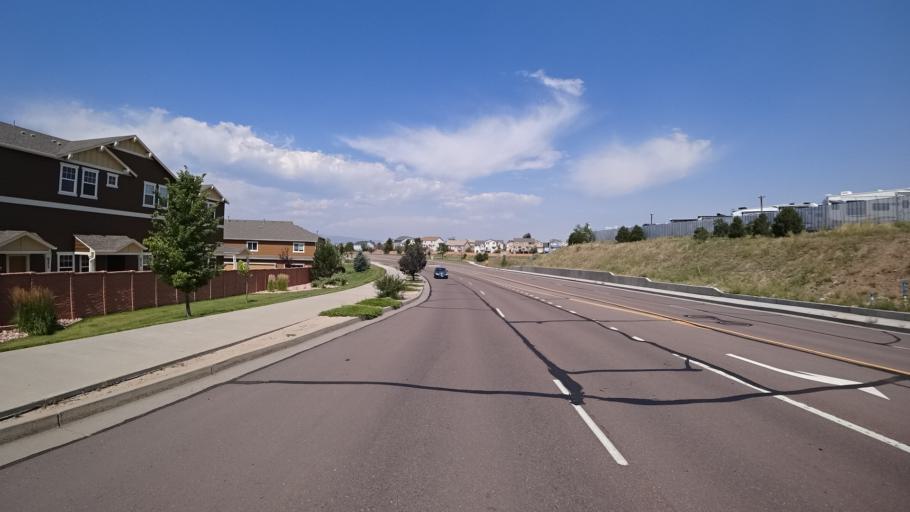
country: US
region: Colorado
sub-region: El Paso County
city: Cimarron Hills
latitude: 38.9286
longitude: -104.7242
